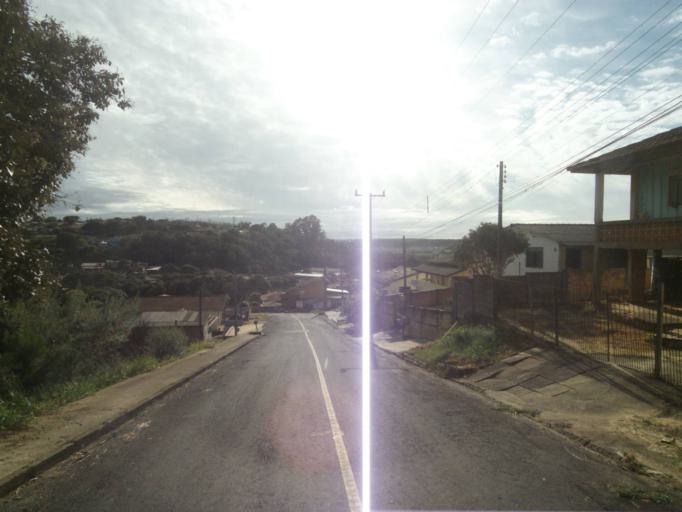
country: BR
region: Parana
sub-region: Telemaco Borba
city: Telemaco Borba
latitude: -24.3417
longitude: -50.6170
